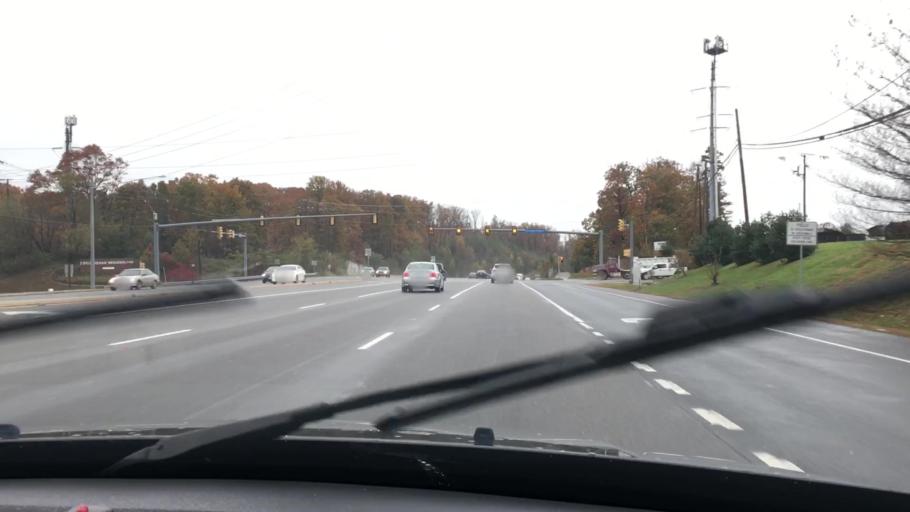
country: US
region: Virginia
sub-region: Fairfax County
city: Lorton
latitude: 38.6944
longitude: -77.2564
